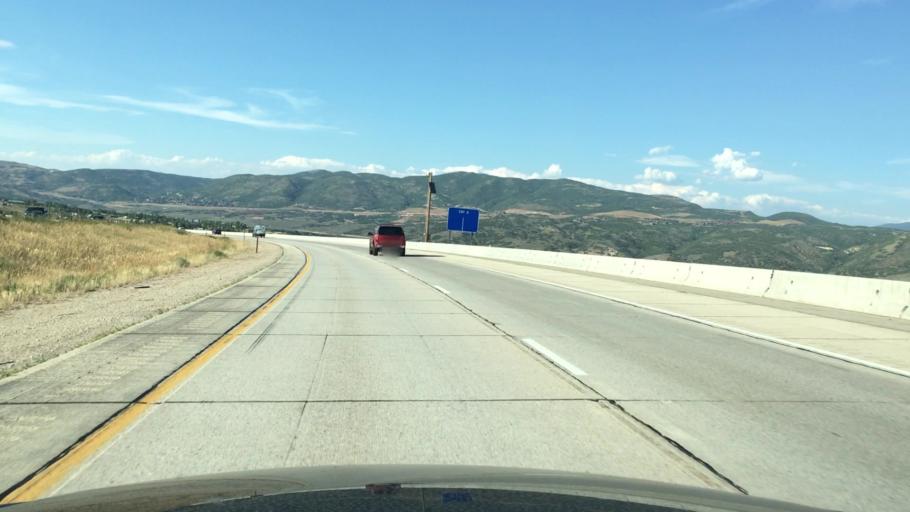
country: US
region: Utah
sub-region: Summit County
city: Park City
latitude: 40.6038
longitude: -111.4294
